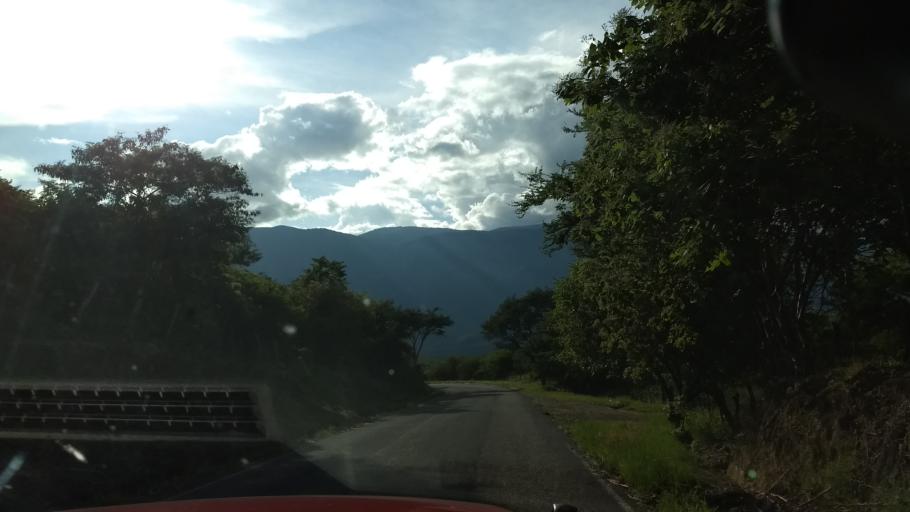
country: MX
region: Colima
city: Suchitlan
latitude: 19.4585
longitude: -103.7964
